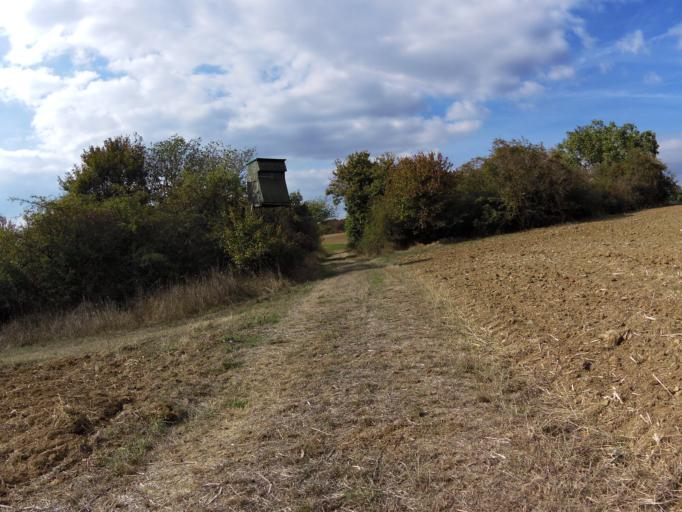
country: DE
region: Bavaria
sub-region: Regierungsbezirk Unterfranken
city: Hettstadt
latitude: 49.7869
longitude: 9.7970
